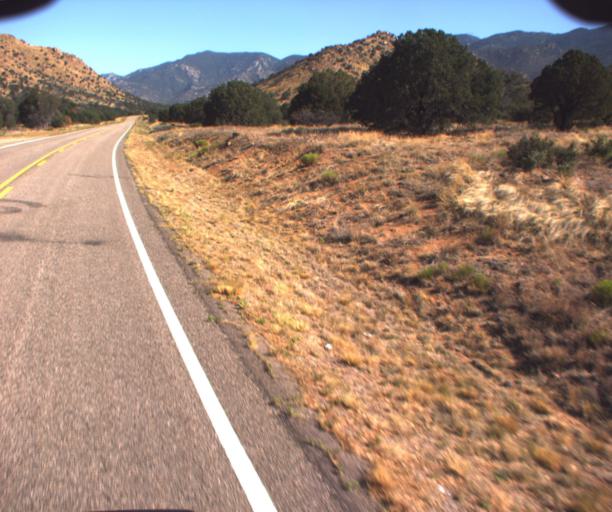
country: US
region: Arizona
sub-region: Graham County
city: Swift Trail Junction
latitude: 32.5791
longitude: -109.8499
